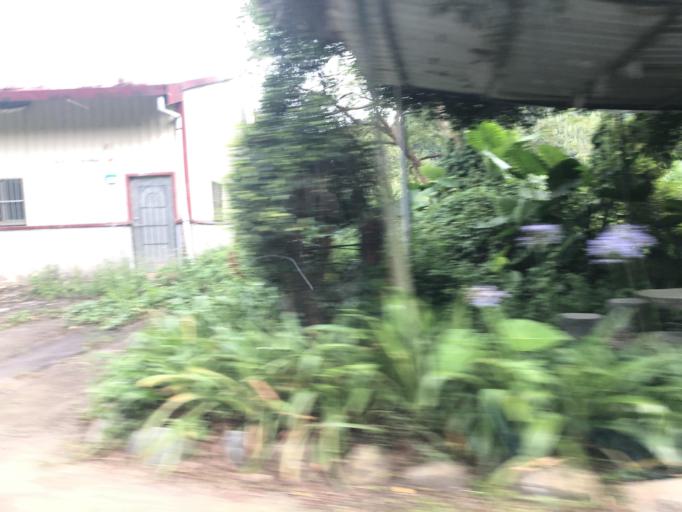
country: TW
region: Taiwan
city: Daxi
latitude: 24.9147
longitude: 121.3456
